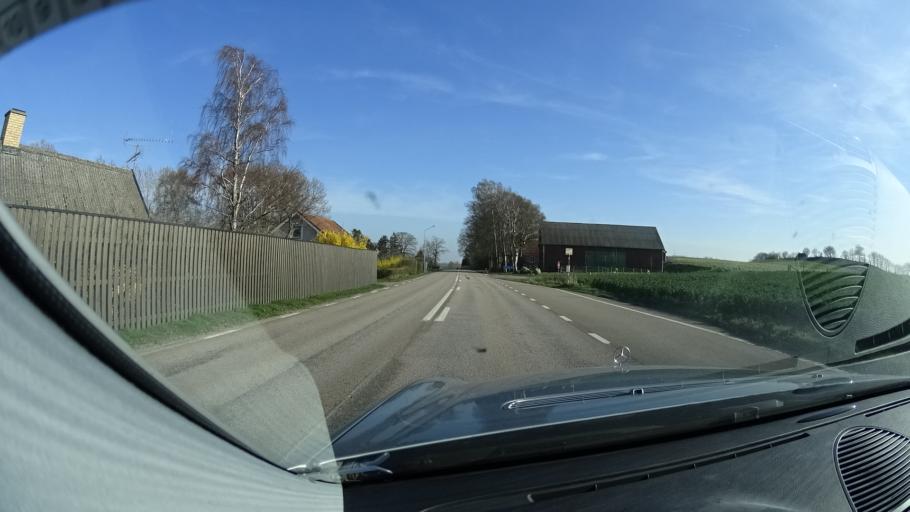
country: SE
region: Skane
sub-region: Landskrona
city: Asmundtorp
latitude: 55.9378
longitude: 12.9495
